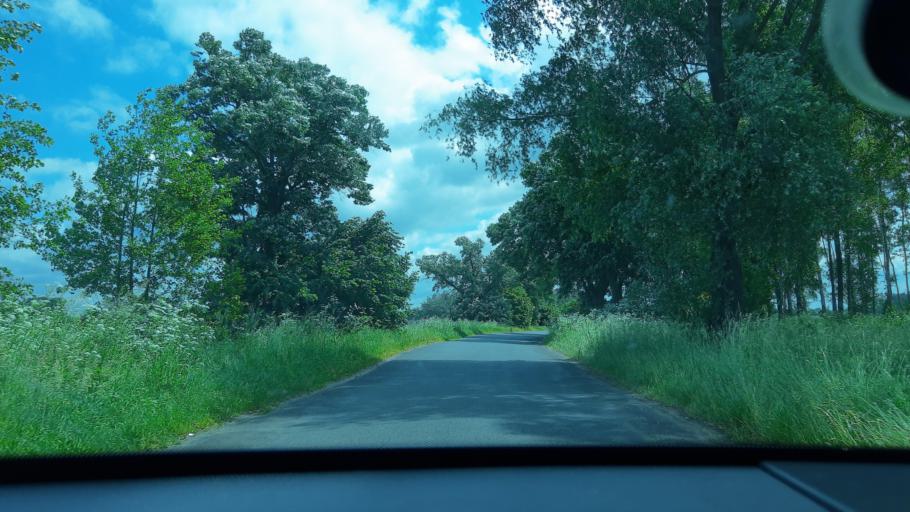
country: PL
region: Lodz Voivodeship
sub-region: Powiat zdunskowolski
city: Zapolice
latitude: 51.5394
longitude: 18.8219
